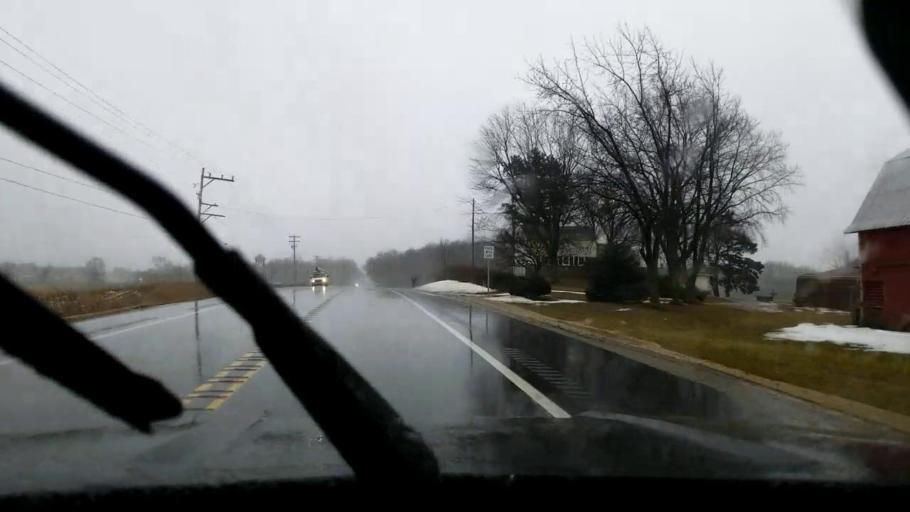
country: US
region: Michigan
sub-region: Jackson County
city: Napoleon
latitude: 42.1813
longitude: -84.2934
